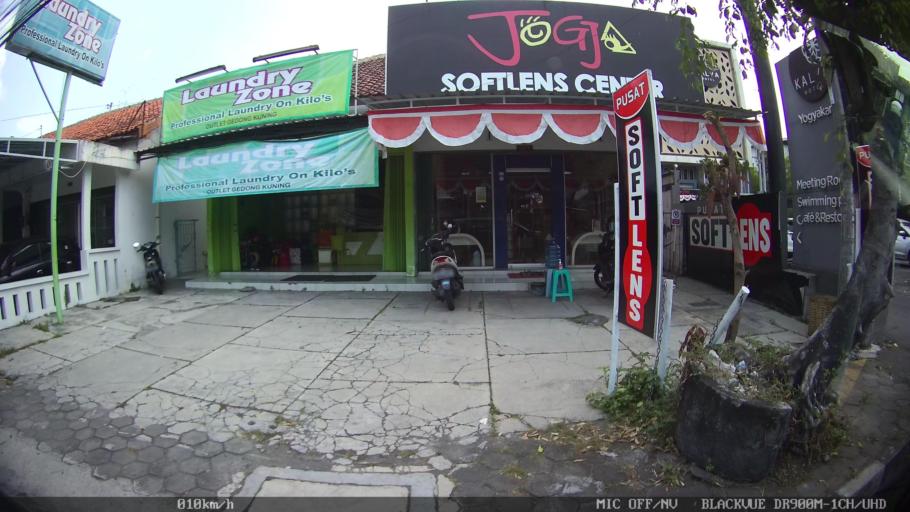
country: ID
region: Daerah Istimewa Yogyakarta
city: Yogyakarta
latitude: -7.8138
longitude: 110.4020
